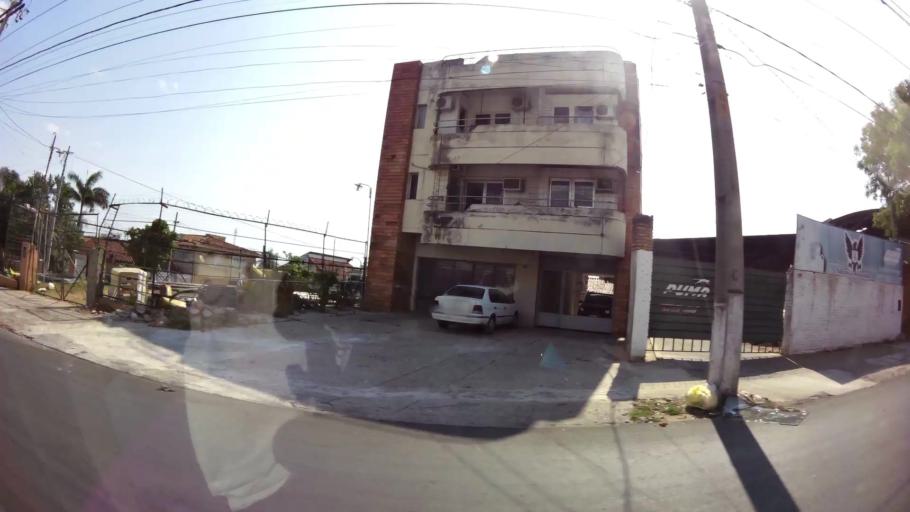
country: PY
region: Asuncion
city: Asuncion
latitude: -25.3026
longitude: -57.6324
